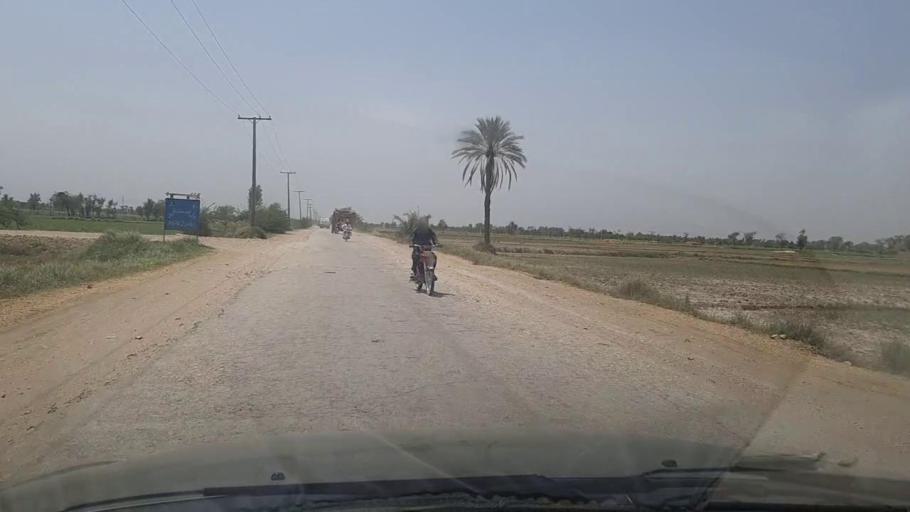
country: PK
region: Sindh
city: Bhiria
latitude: 26.8909
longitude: 68.2588
